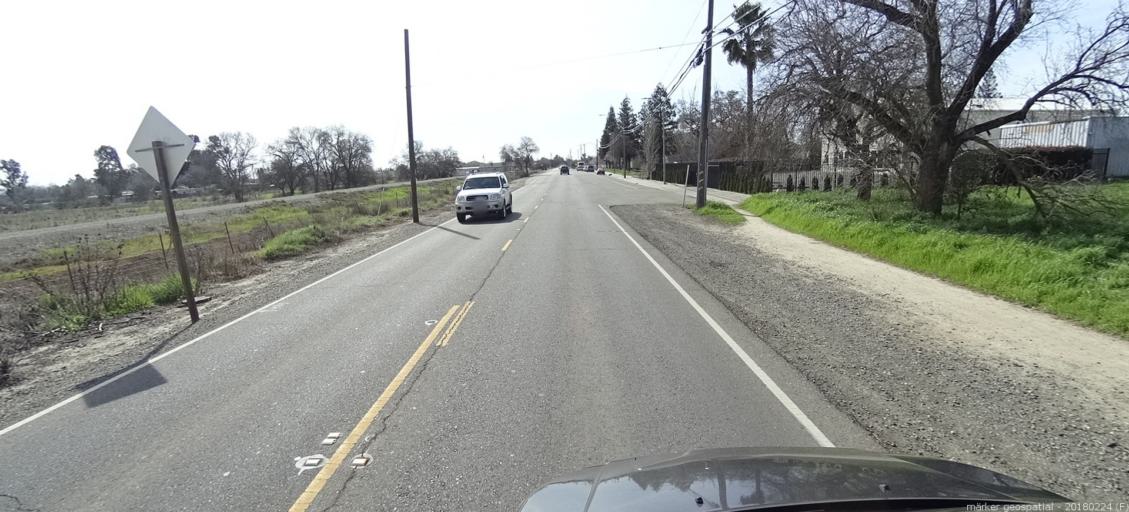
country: US
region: California
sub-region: Sacramento County
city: Rio Linda
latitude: 38.6751
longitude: -121.4384
